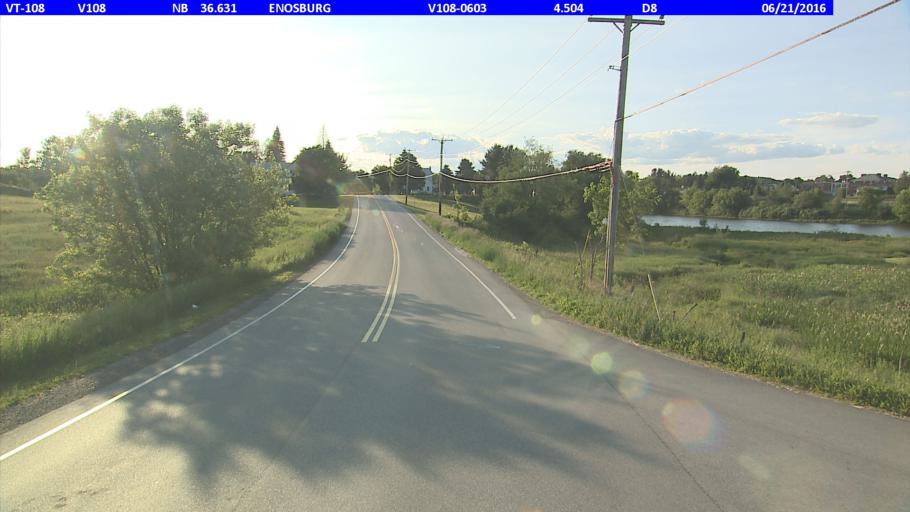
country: US
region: Vermont
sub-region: Franklin County
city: Enosburg Falls
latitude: 44.9002
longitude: -72.8031
